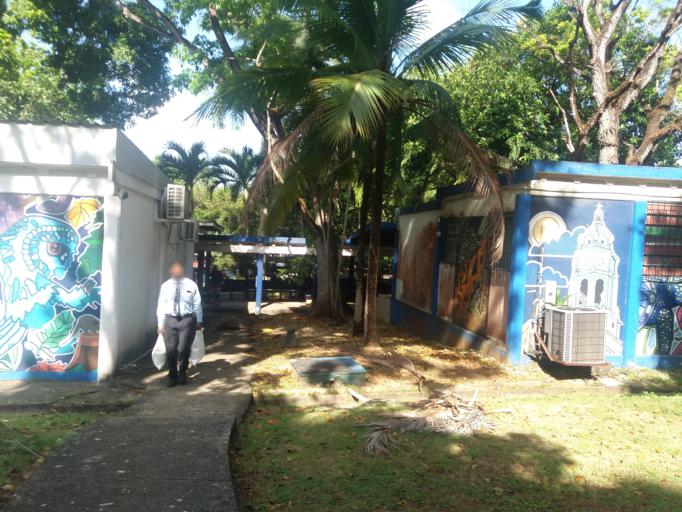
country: PA
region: Panama
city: Panama
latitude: 8.9844
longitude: -79.5335
